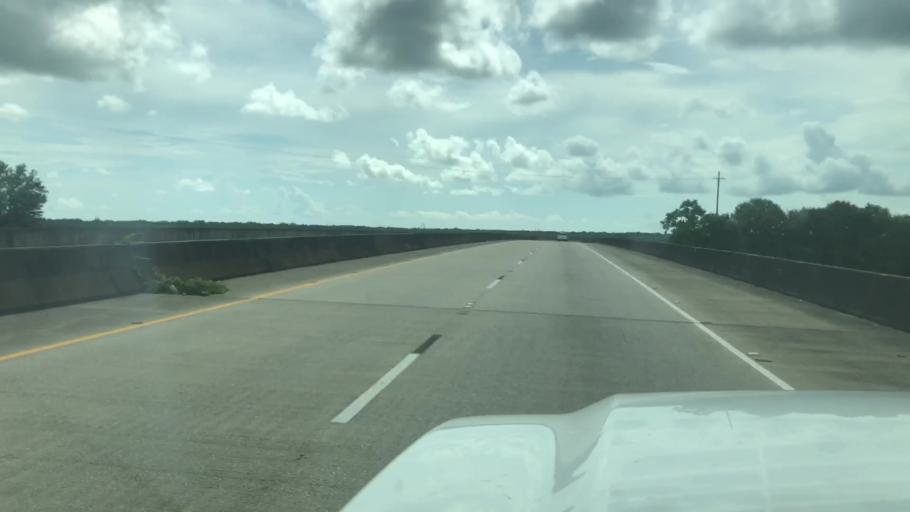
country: US
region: Louisiana
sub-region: Saint Mary Parish
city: Franklin
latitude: 29.7581
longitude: -91.4647
